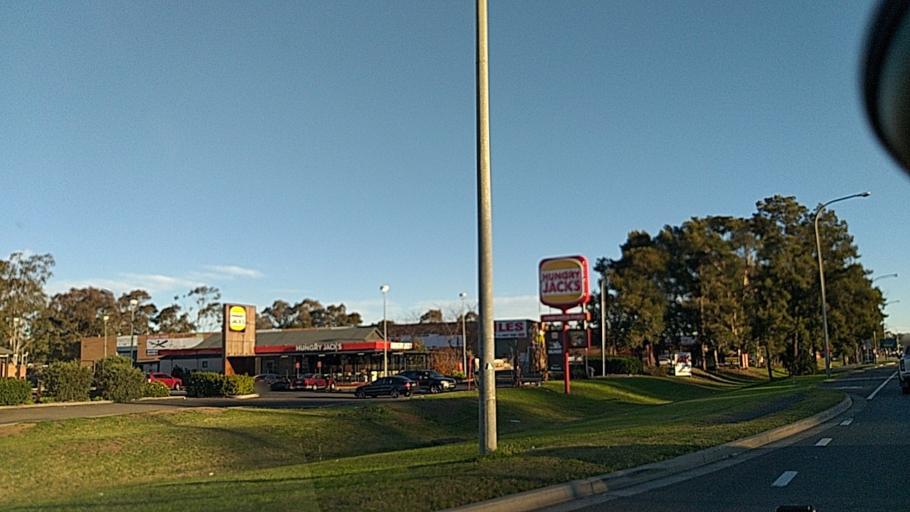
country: AU
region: New South Wales
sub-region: Campbelltown Municipality
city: Leumeah
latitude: -34.0497
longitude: 150.8268
